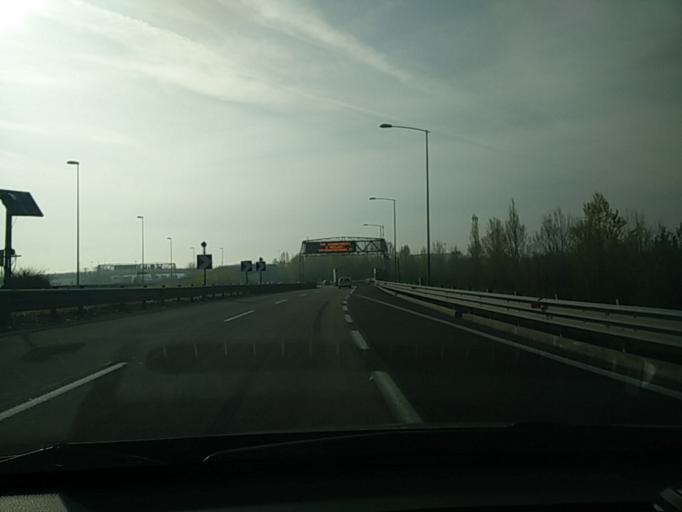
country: IT
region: Emilia-Romagna
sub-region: Provincia di Bologna
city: Bologna
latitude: 44.5208
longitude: 11.3676
